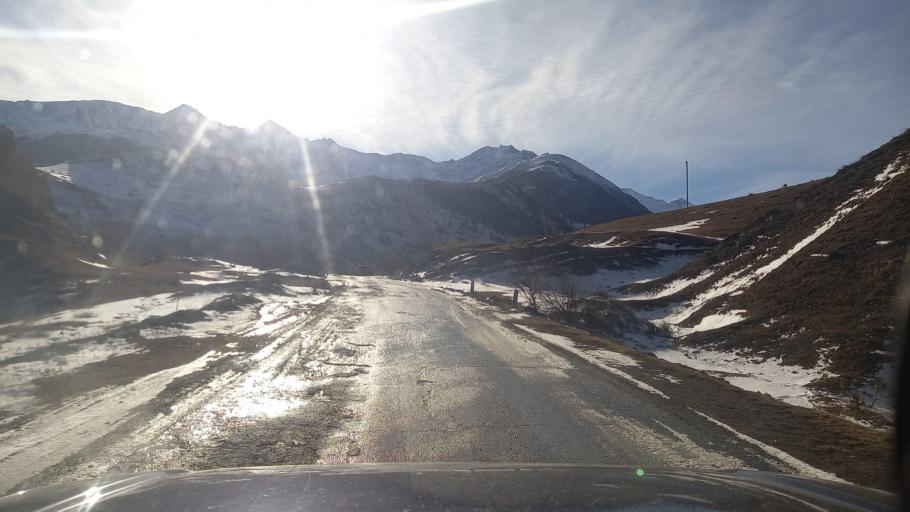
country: RU
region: Ingushetiya
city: Dzhayrakh
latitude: 42.8458
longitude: 44.5153
